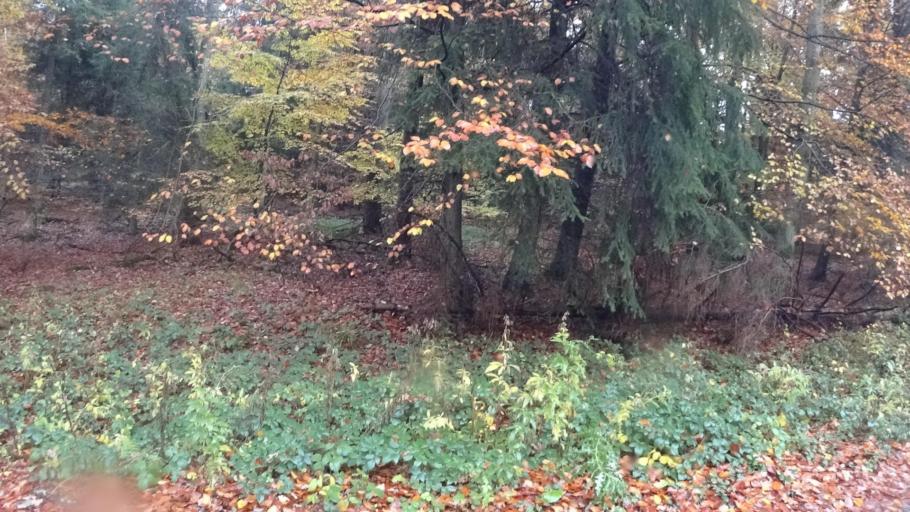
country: DE
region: Rheinland-Pfalz
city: Bickenbach
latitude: 50.1043
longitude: 7.5266
